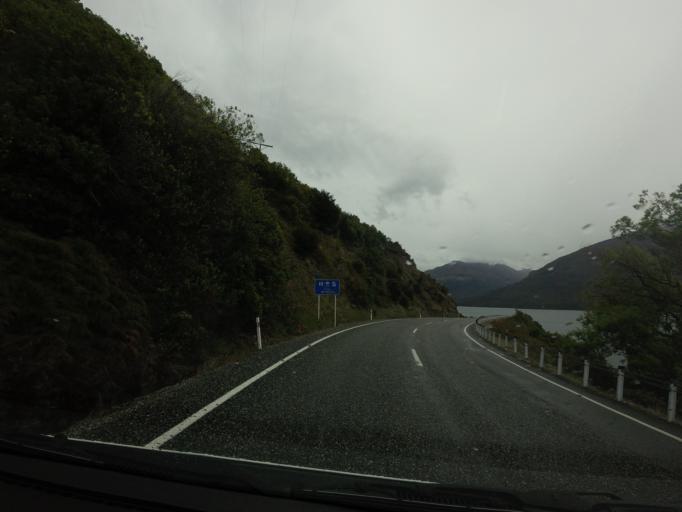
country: NZ
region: Otago
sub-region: Queenstown-Lakes District
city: Wanaka
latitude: -44.3370
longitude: 169.1794
